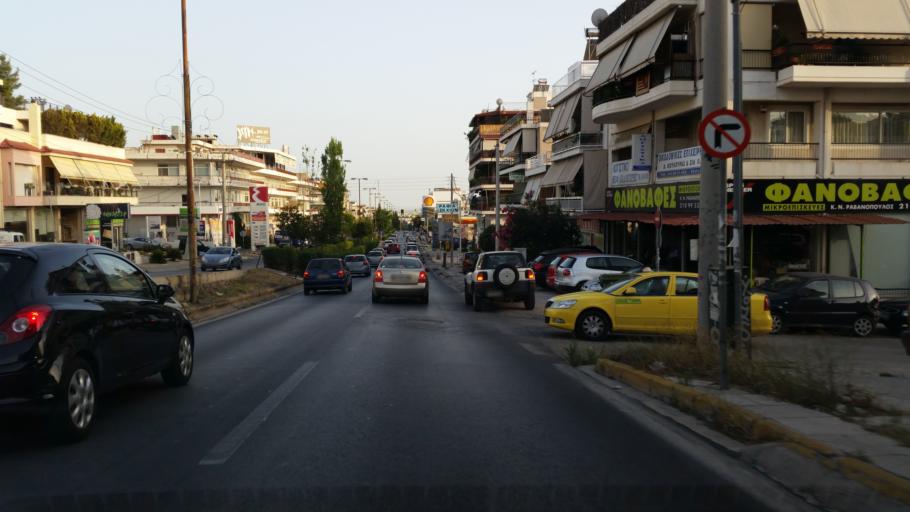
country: GR
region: Attica
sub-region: Nomarchia Athinas
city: Argyroupoli
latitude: 37.9163
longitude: 23.7548
